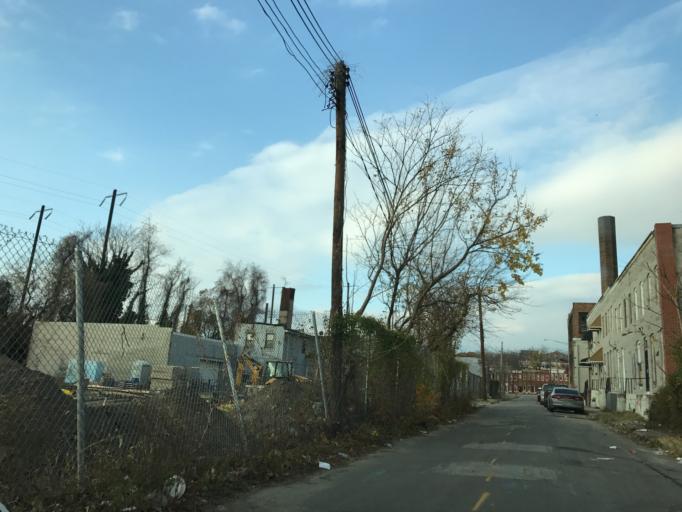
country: US
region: Maryland
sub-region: City of Baltimore
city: Baltimore
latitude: 39.3070
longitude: -76.5927
